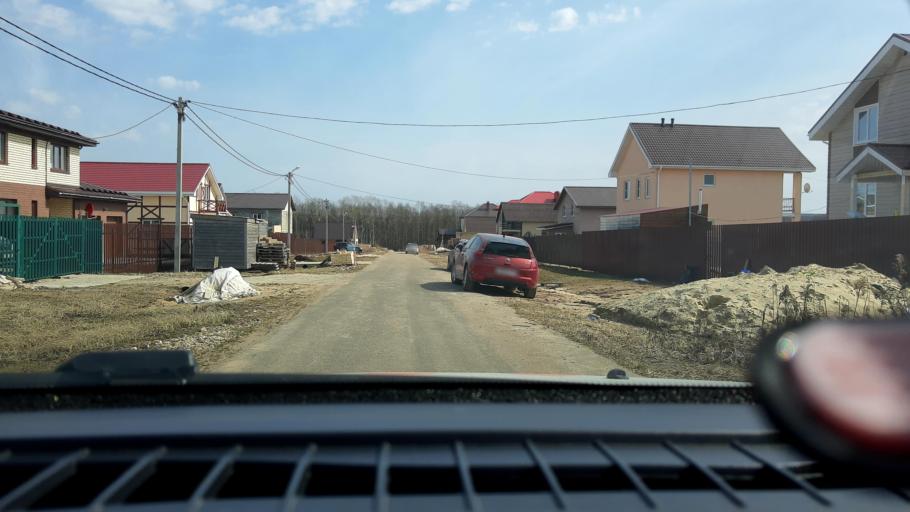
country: RU
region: Nizjnij Novgorod
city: Burevestnik
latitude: 56.0440
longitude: 43.8429
